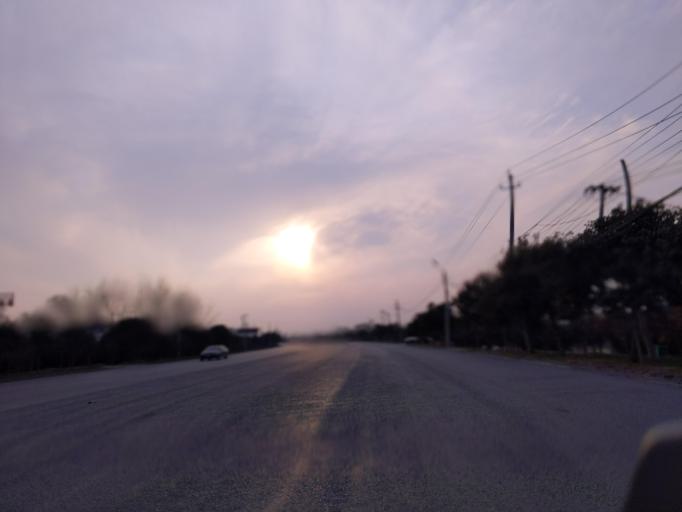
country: CN
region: Henan Sheng
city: Puyang
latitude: 35.8200
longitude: 114.9761
